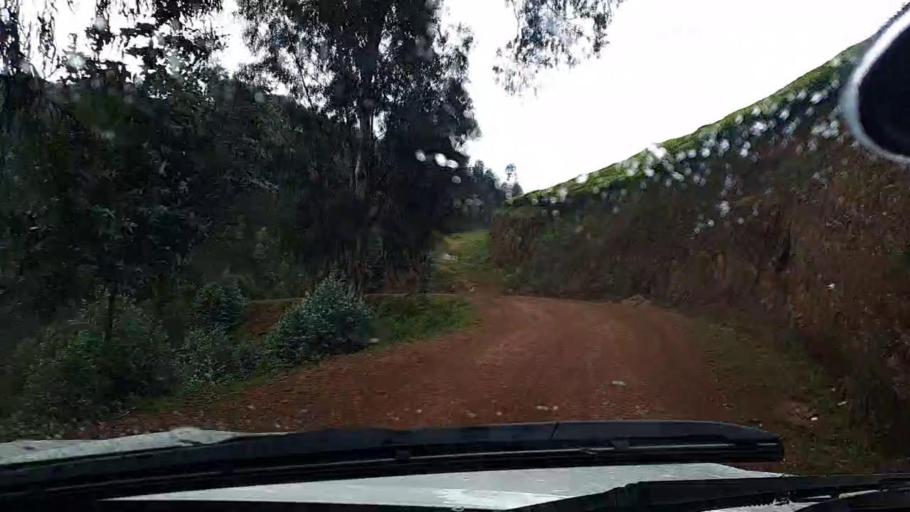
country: RW
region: Western Province
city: Kibuye
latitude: -2.1629
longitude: 29.4346
